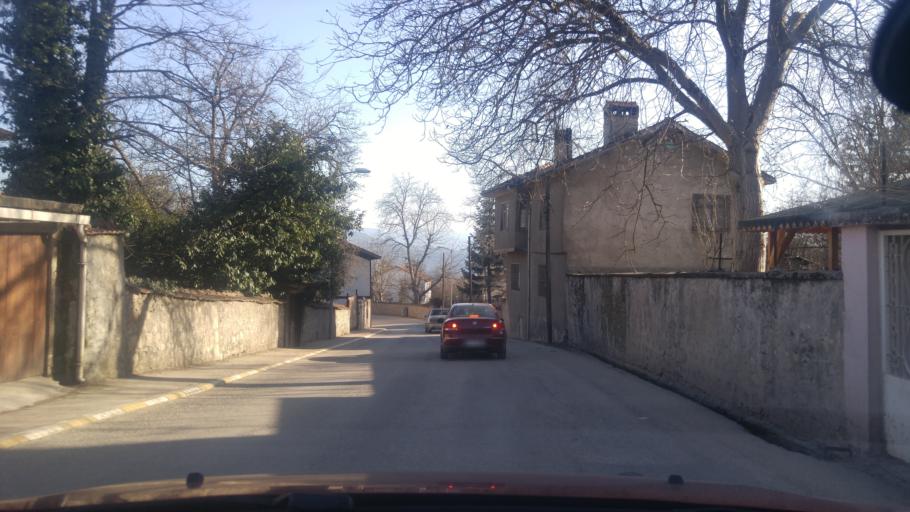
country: TR
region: Karabuk
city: Safranbolu
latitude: 41.2614
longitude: 32.6705
